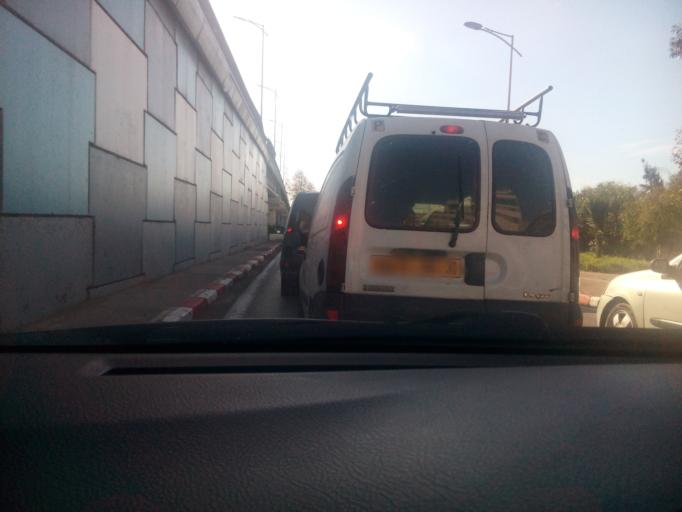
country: DZ
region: Oran
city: Oran
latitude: 35.6851
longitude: -0.6097
